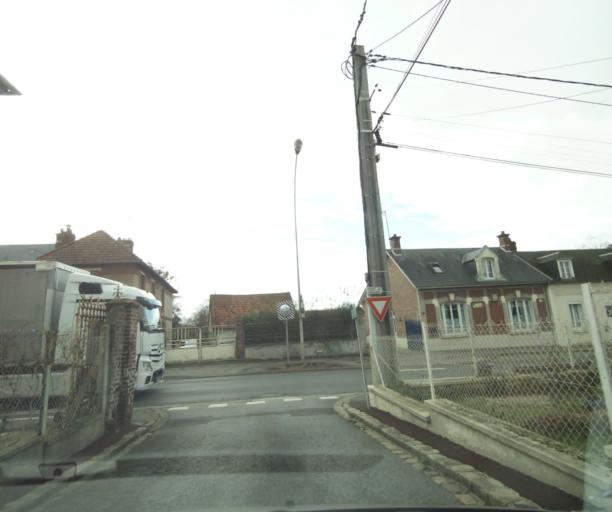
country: FR
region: Picardie
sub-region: Departement de l'Oise
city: Noyon
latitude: 49.5846
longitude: 2.9955
